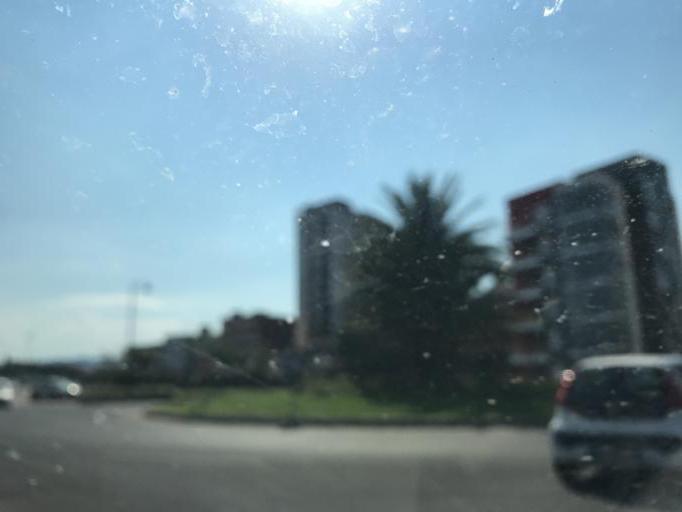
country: IT
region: Sardinia
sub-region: Provincia di Olbia-Tempio
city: Olbia
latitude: 40.9220
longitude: 9.5046
